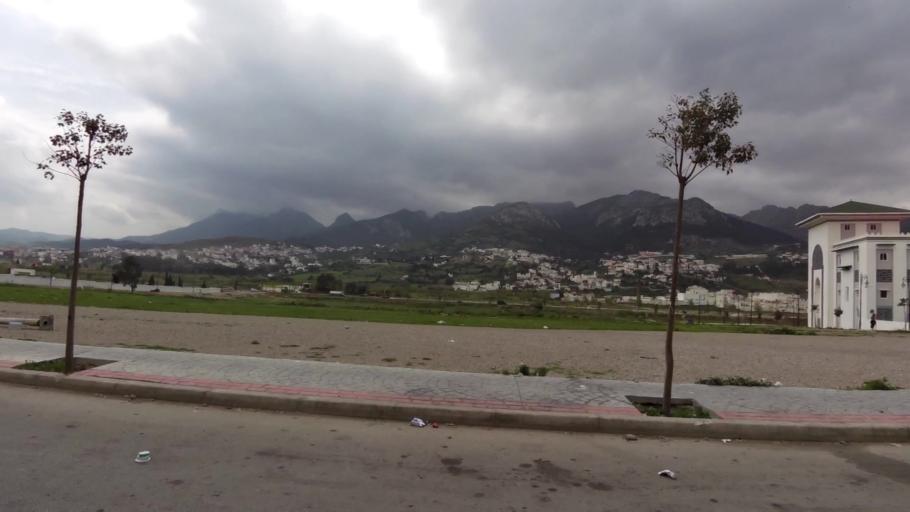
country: MA
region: Tanger-Tetouan
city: Tetouan
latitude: 35.5623
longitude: -5.3663
